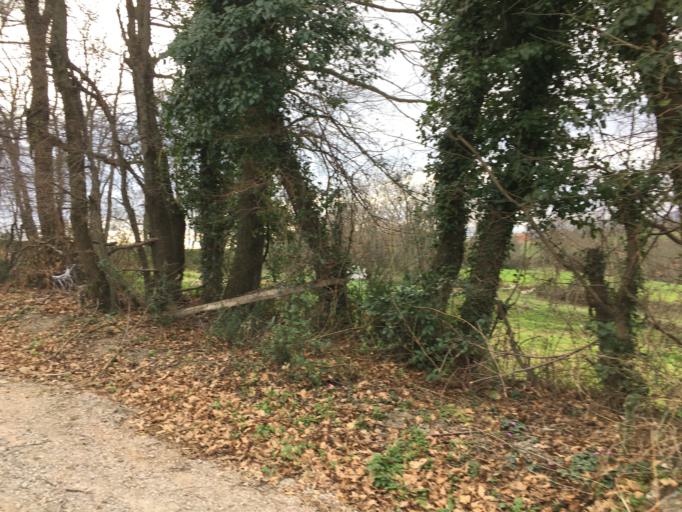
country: TR
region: Samsun
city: Alacam
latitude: 41.6007
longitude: 35.6094
